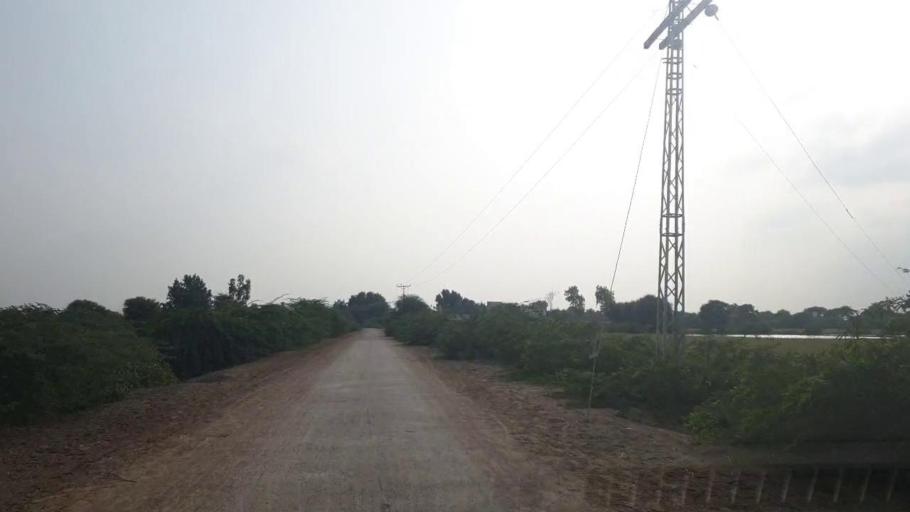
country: PK
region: Sindh
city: Badin
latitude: 24.6130
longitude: 68.6857
